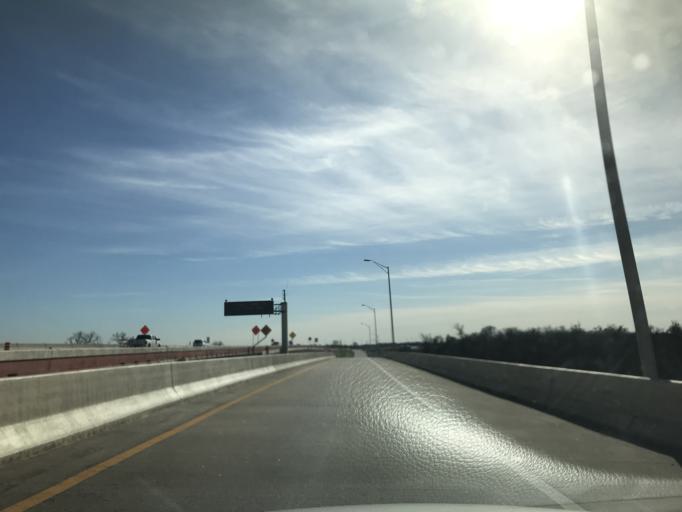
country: US
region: Texas
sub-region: Dallas County
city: Carrollton
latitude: 32.9720
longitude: -96.9332
